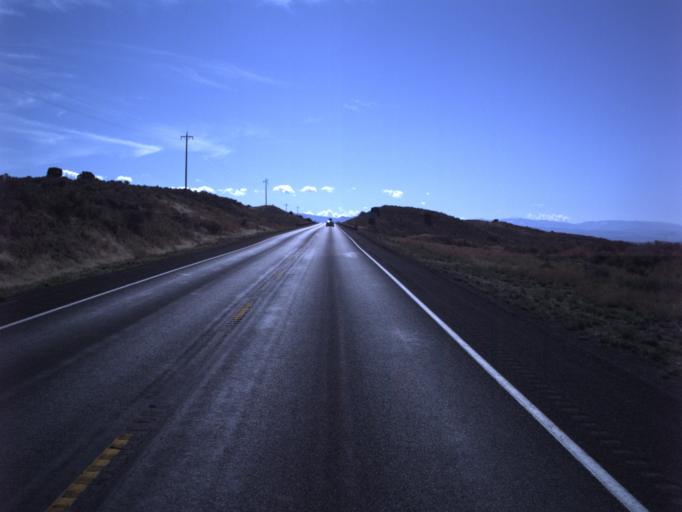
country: US
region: Utah
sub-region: Sanpete County
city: Gunnison
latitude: 39.2872
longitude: -111.8841
